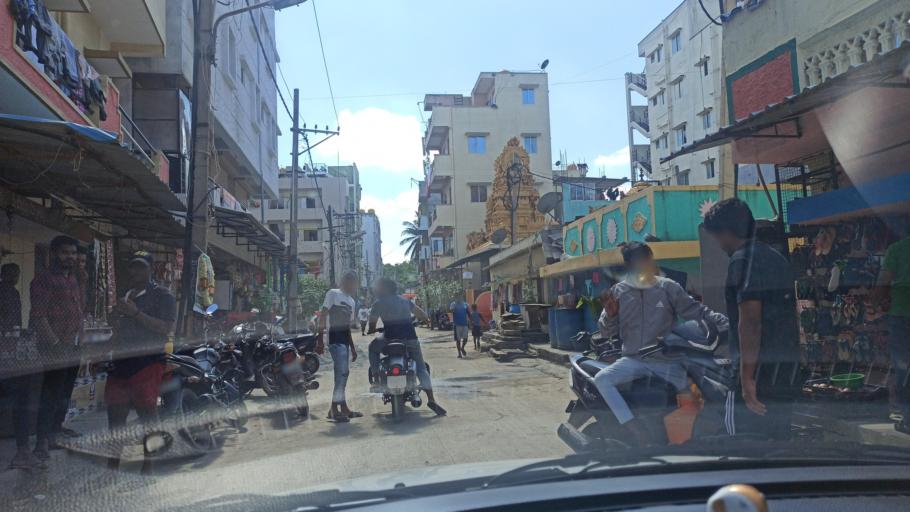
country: IN
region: Karnataka
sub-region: Bangalore Urban
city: Bangalore
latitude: 12.9230
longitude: 77.6631
